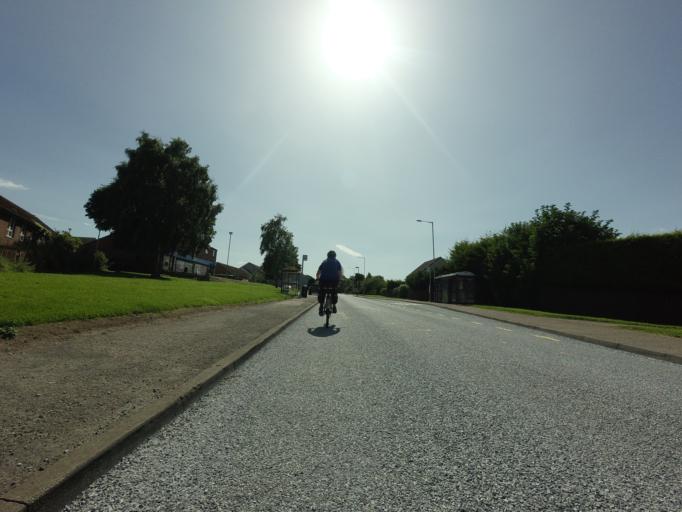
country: GB
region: Scotland
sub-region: Highland
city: Inverness
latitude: 57.4810
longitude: -4.1507
